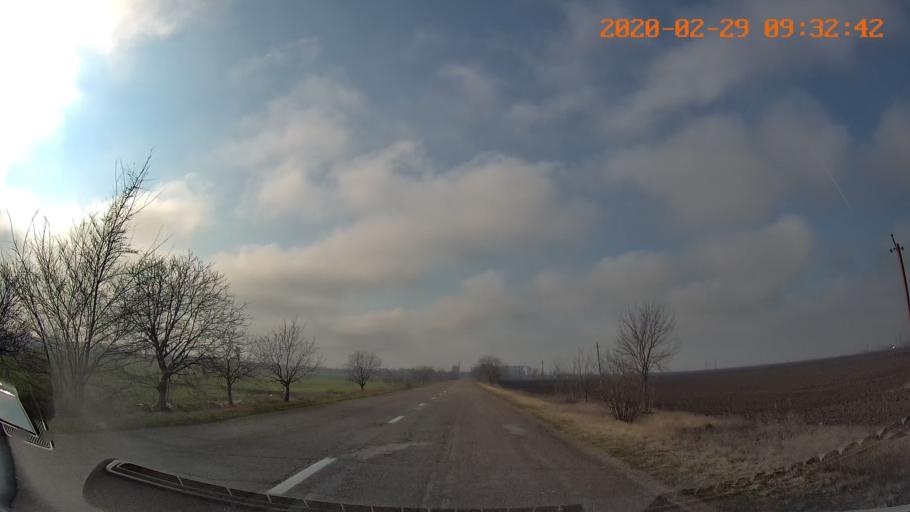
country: MD
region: Telenesti
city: Dnestrovsc
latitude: 46.6361
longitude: 29.9047
